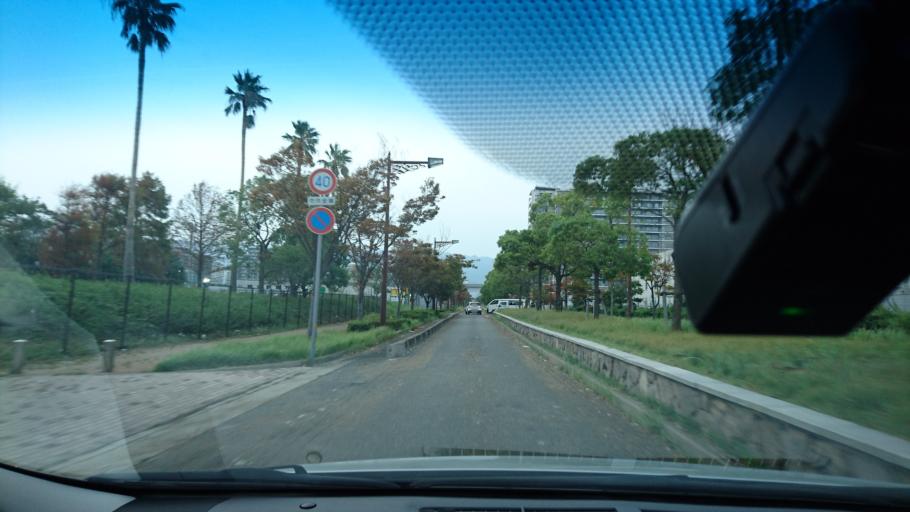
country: JP
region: Hyogo
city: Ashiya
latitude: 34.6805
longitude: 135.2686
